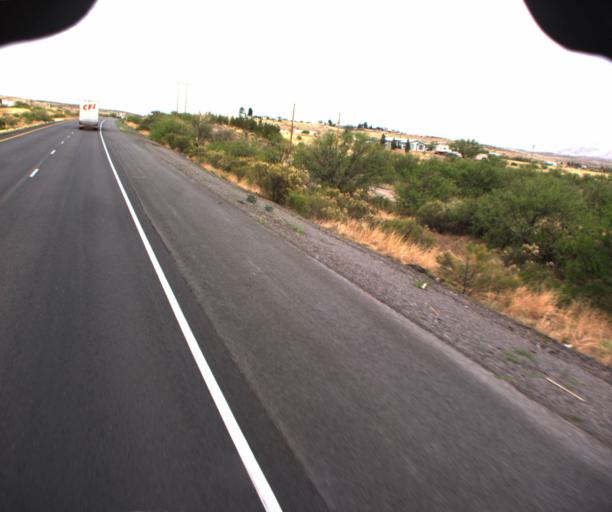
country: US
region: Arizona
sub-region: Cochise County
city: Mescal
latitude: 31.9637
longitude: -110.4523
